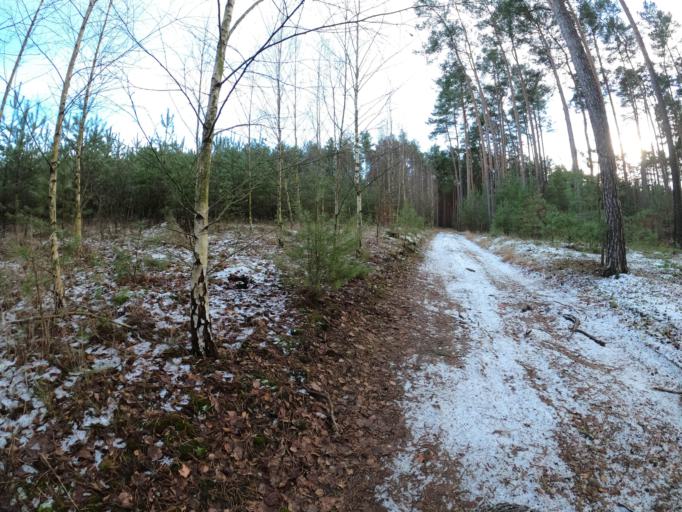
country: PL
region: Lubusz
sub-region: Powiat slubicki
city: Cybinka
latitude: 52.2188
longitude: 14.8365
